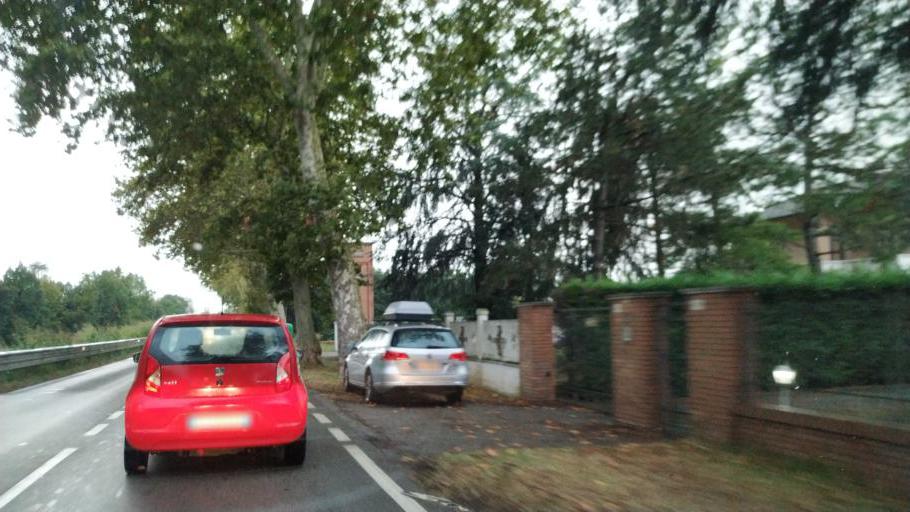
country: IT
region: Emilia-Romagna
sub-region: Provincia di Ferrara
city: Pontegradella
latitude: 44.8469
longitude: 11.6582
